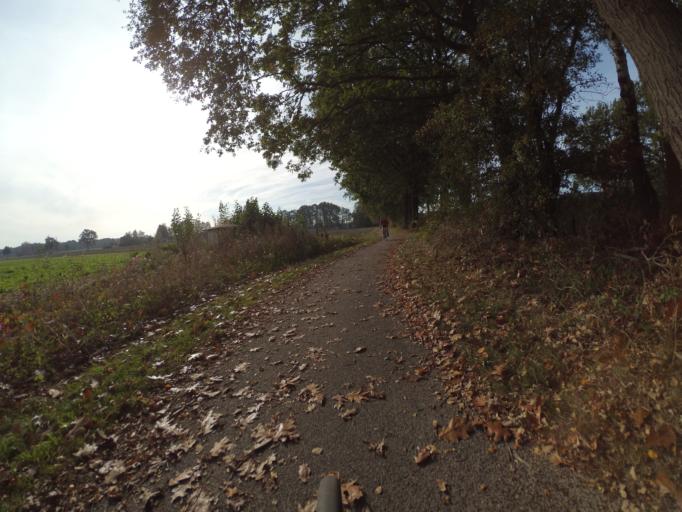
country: NL
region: Overijssel
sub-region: Gemeente Raalte
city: Raalte
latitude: 52.3215
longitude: 6.2641
